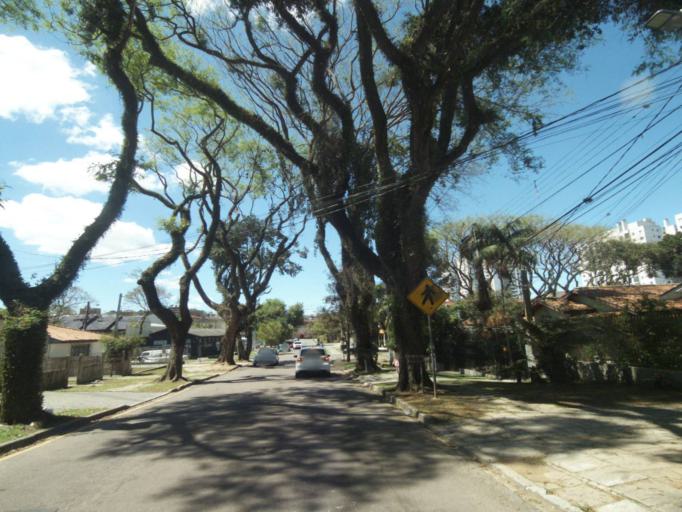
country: BR
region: Parana
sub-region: Curitiba
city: Curitiba
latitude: -25.3891
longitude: -49.2393
